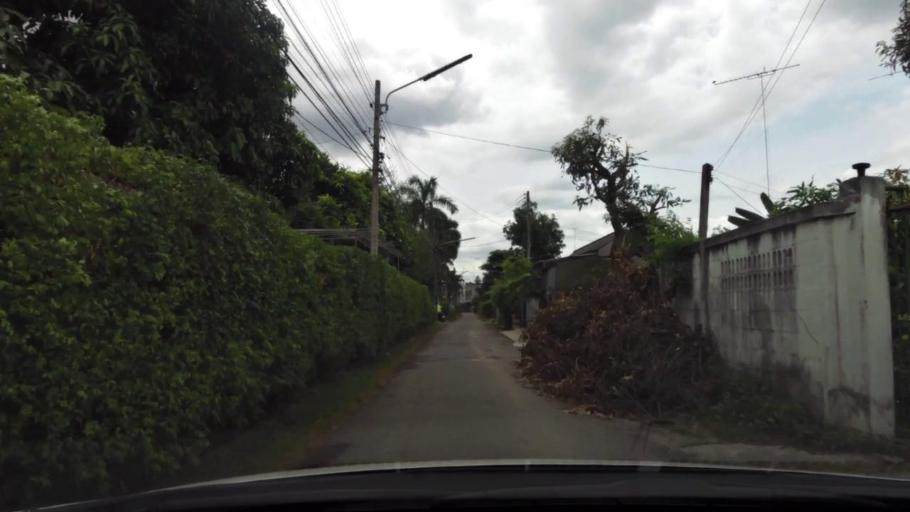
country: TH
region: Ratchaburi
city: Ratchaburi
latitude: 13.5322
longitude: 99.8269
